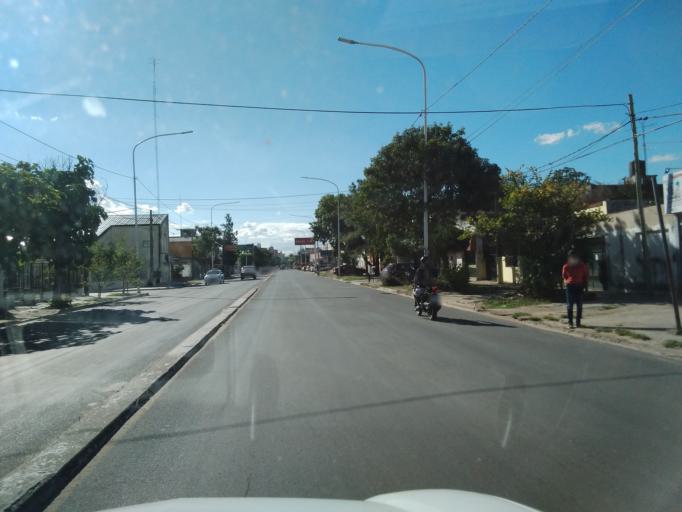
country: AR
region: Corrientes
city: Corrientes
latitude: -27.4823
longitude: -58.8264
